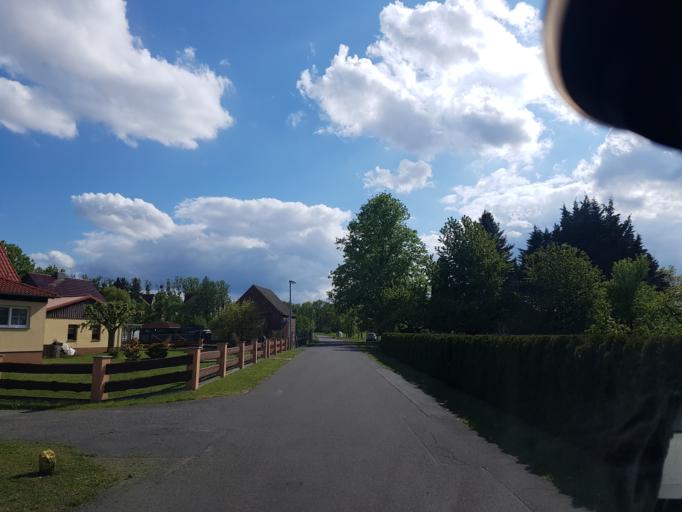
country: DE
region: Brandenburg
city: Drebkau
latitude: 51.6416
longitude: 14.2407
